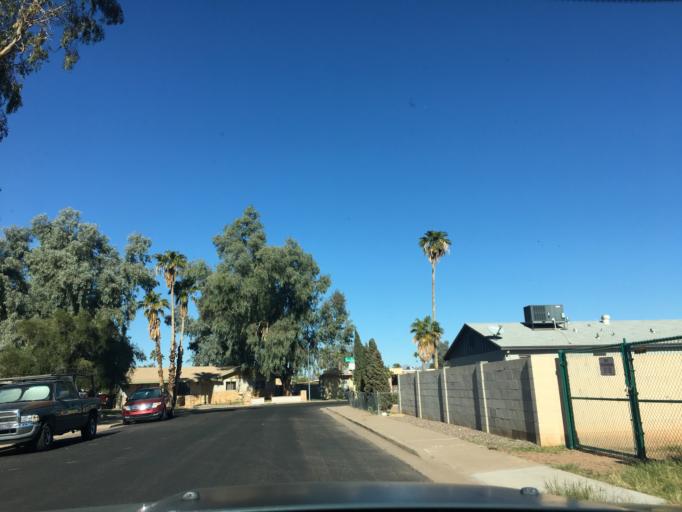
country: US
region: Arizona
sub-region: Maricopa County
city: Mesa
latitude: 33.4469
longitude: -111.8468
